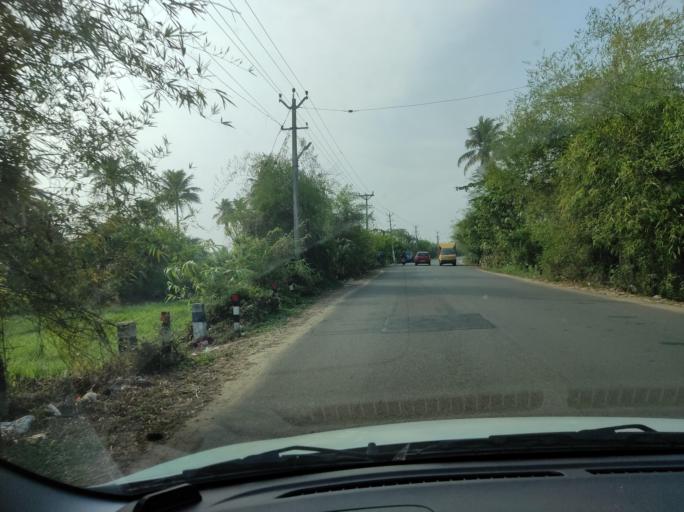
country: IN
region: Kerala
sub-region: Kottayam
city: Kottayam
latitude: 9.5681
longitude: 76.5039
